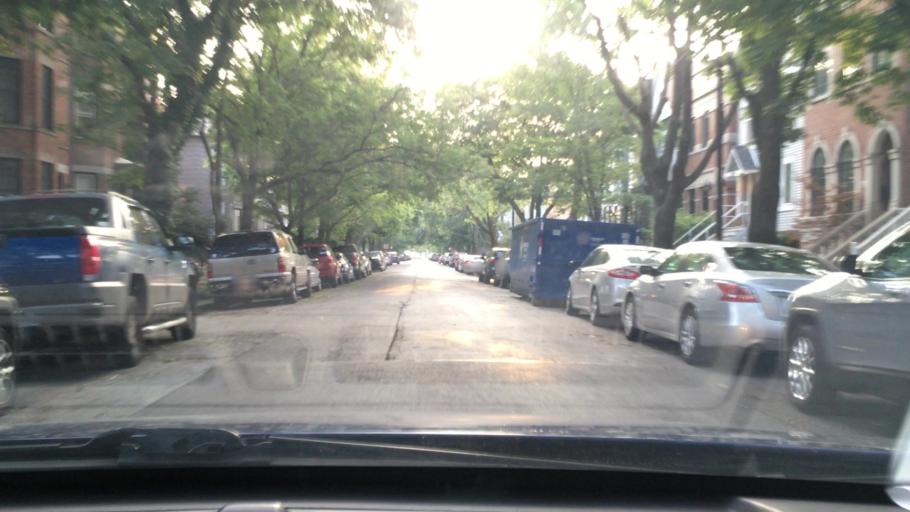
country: US
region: Illinois
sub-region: Cook County
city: Chicago
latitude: 41.9343
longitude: -87.6640
